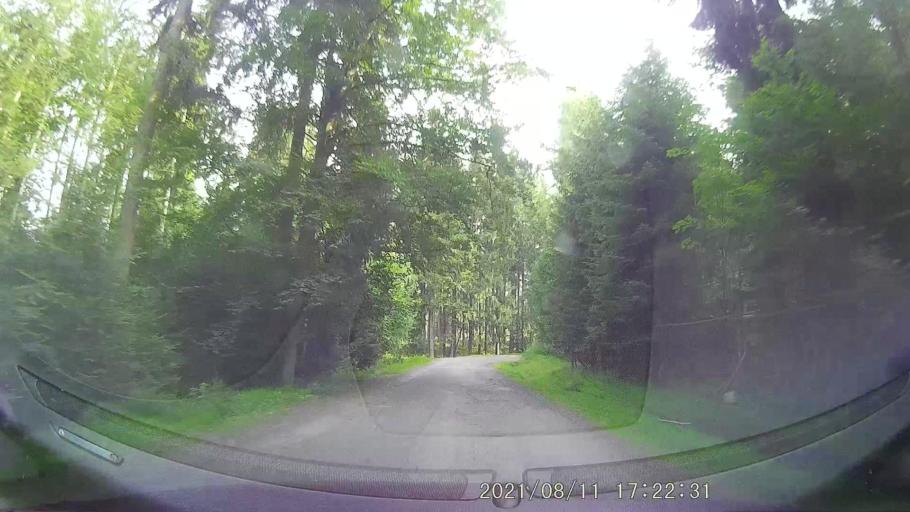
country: PL
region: Lower Silesian Voivodeship
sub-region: Powiat klodzki
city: Polanica-Zdroj
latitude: 50.3075
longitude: 16.5053
